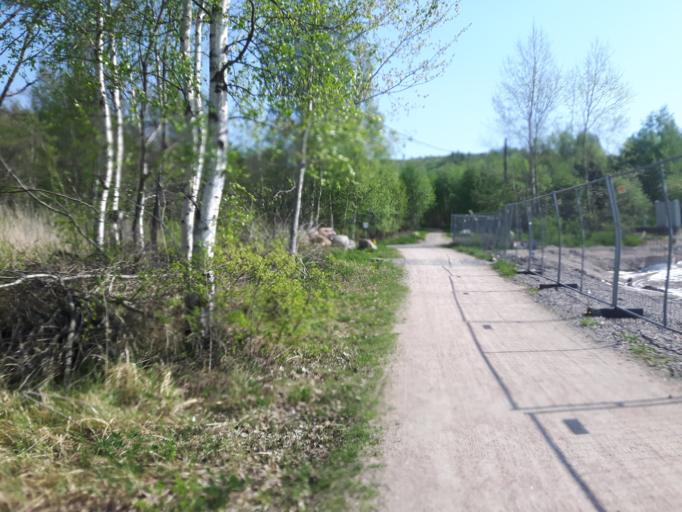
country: FI
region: Uusimaa
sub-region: Helsinki
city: Vantaa
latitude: 60.2288
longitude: 25.1553
